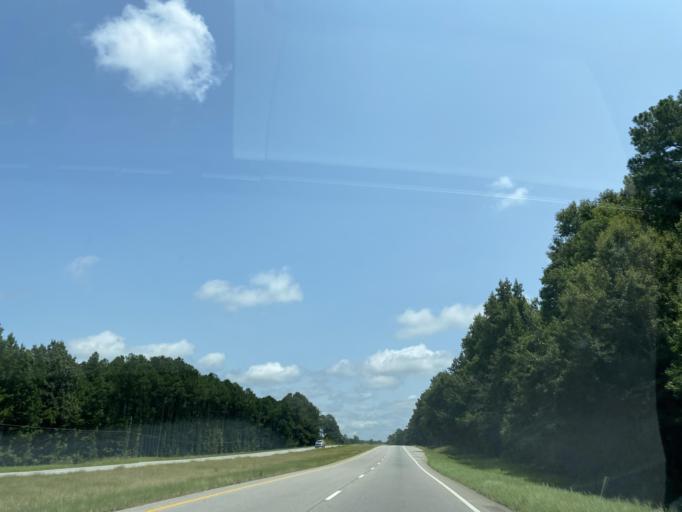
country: US
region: Georgia
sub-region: Telfair County
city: Lumber City
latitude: 31.9056
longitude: -82.6570
